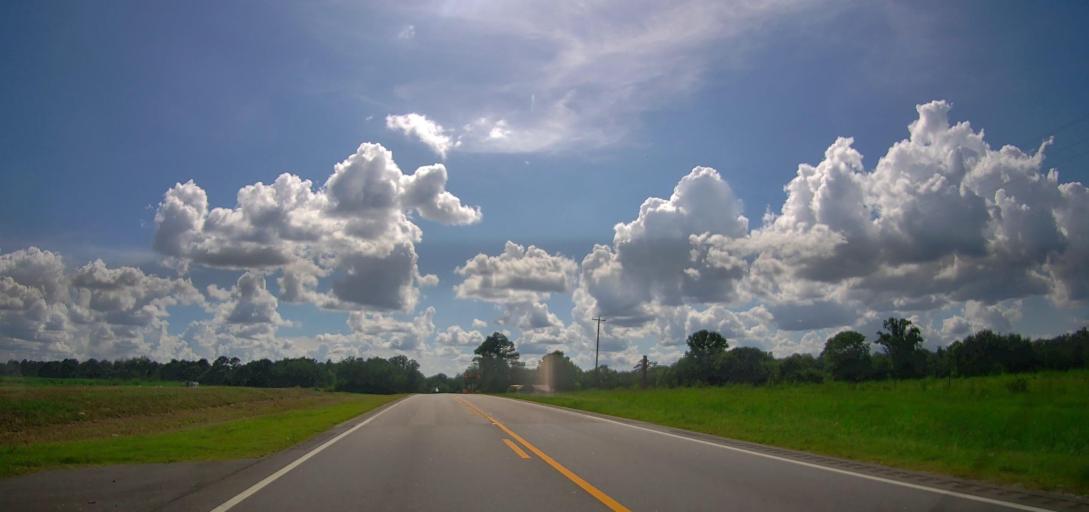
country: US
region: Alabama
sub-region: Lee County
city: Auburn
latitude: 32.4296
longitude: -85.4348
